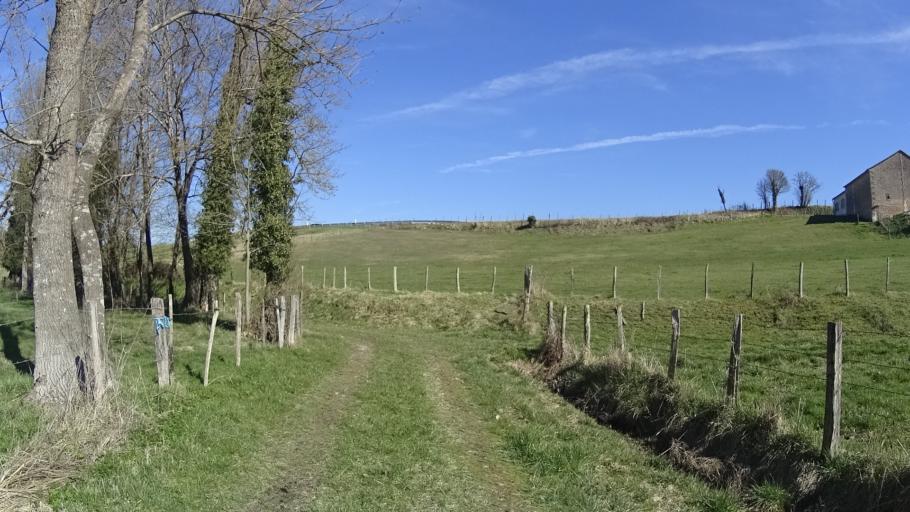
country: FR
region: Aquitaine
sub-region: Departement de la Dordogne
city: Riberac
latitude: 45.2277
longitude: 0.3340
